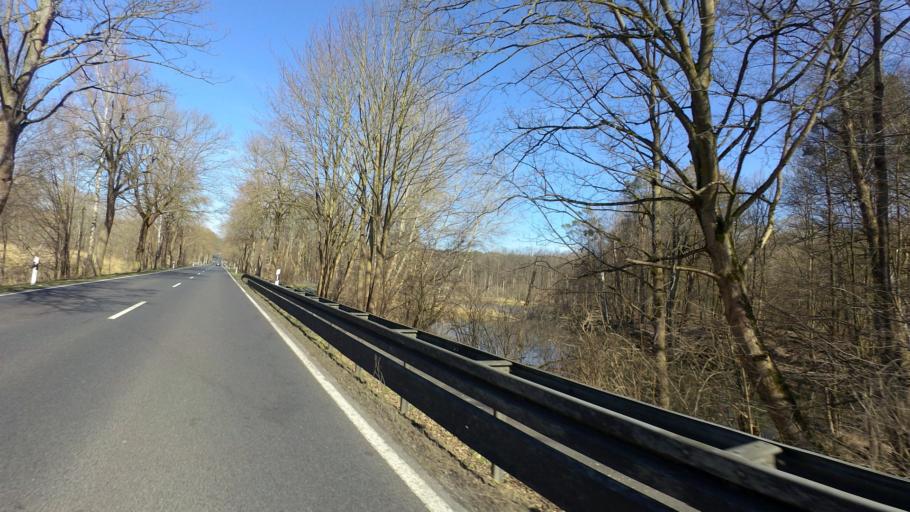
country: DE
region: Brandenburg
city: Chorin
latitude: 52.8745
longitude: 13.8573
